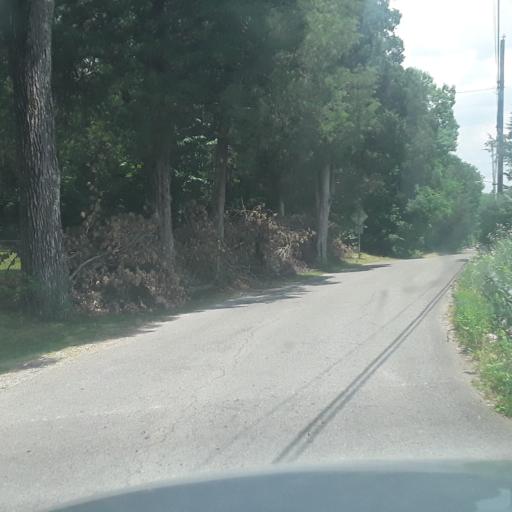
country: US
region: Tennessee
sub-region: Williamson County
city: Brentwood Estates
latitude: 36.0466
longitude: -86.7005
